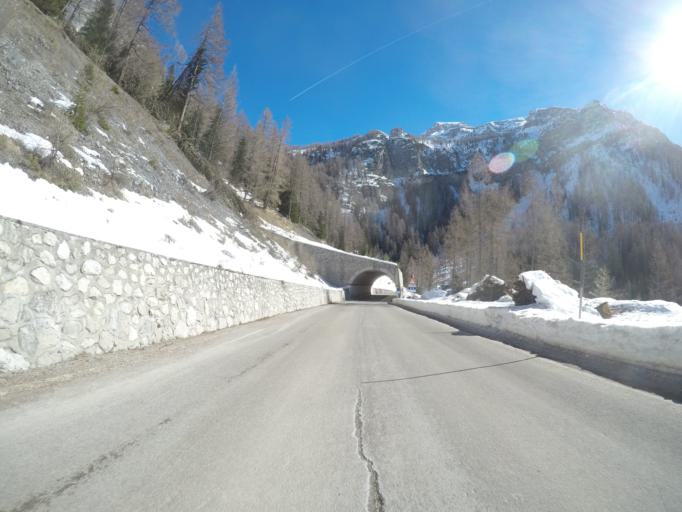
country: IT
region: Veneto
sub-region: Provincia di Belluno
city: Selva di Cadore
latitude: 46.4758
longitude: 12.0368
